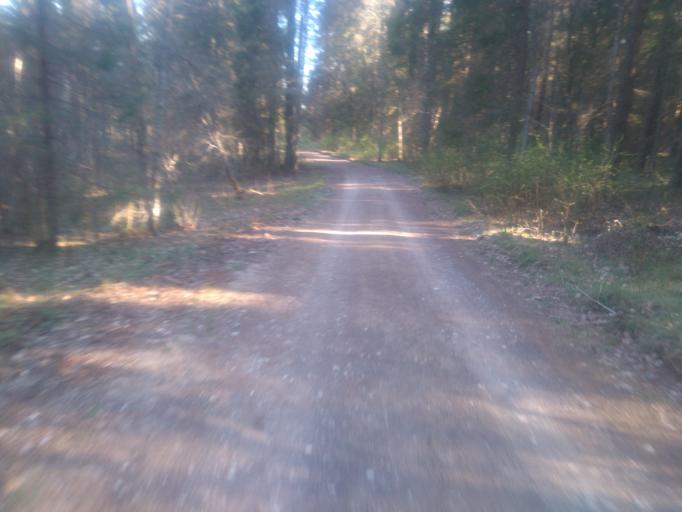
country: LV
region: Vecpiebalga
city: Vecpiebalga
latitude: 57.0084
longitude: 25.8430
